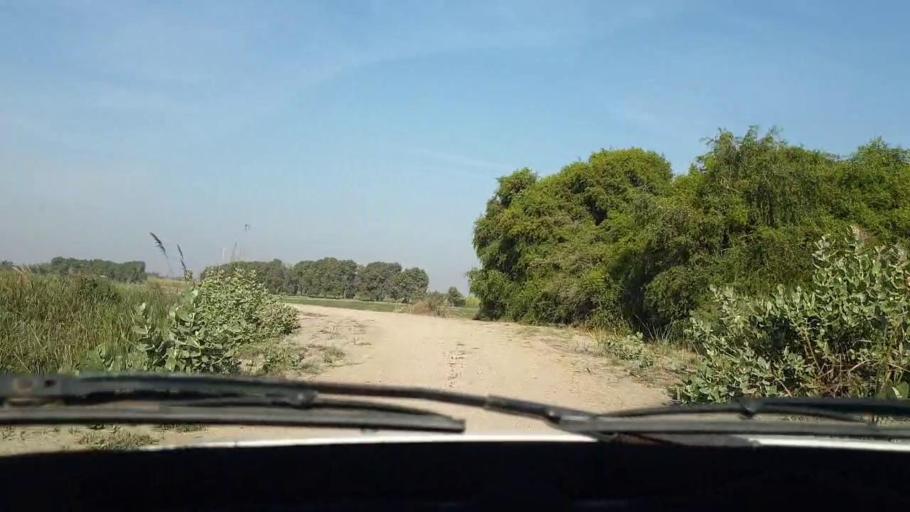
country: PK
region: Sindh
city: Tando Muhammad Khan
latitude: 25.0008
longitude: 68.4596
